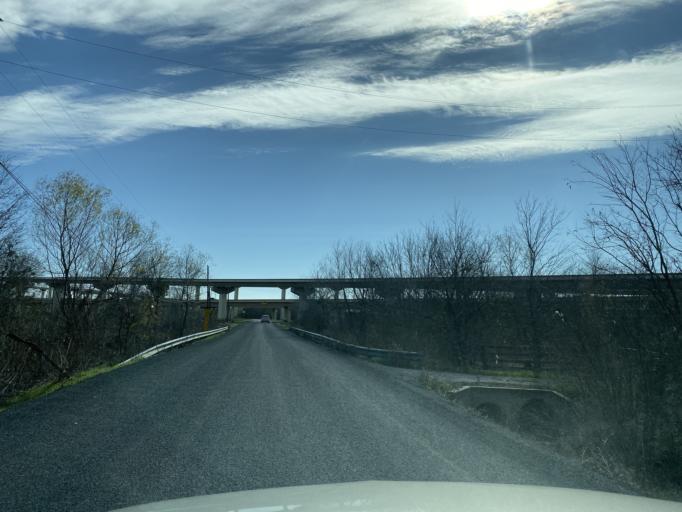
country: US
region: Texas
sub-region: Travis County
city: Onion Creek
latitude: 30.0822
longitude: -97.7005
